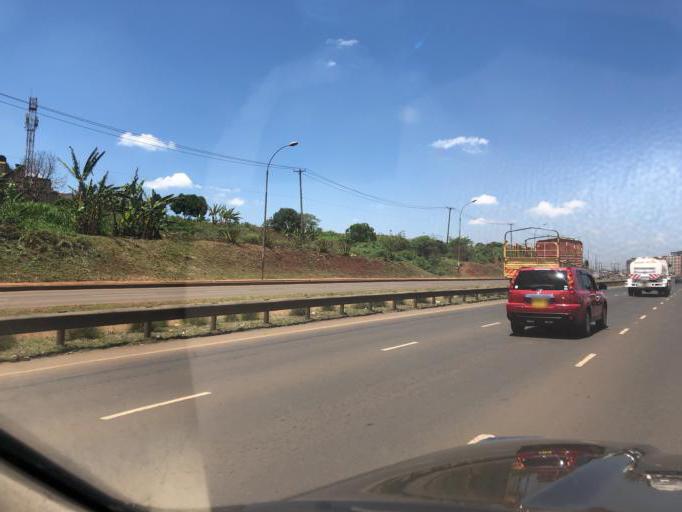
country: KE
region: Kiambu
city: Kiambu
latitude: -1.2133
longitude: 36.9006
